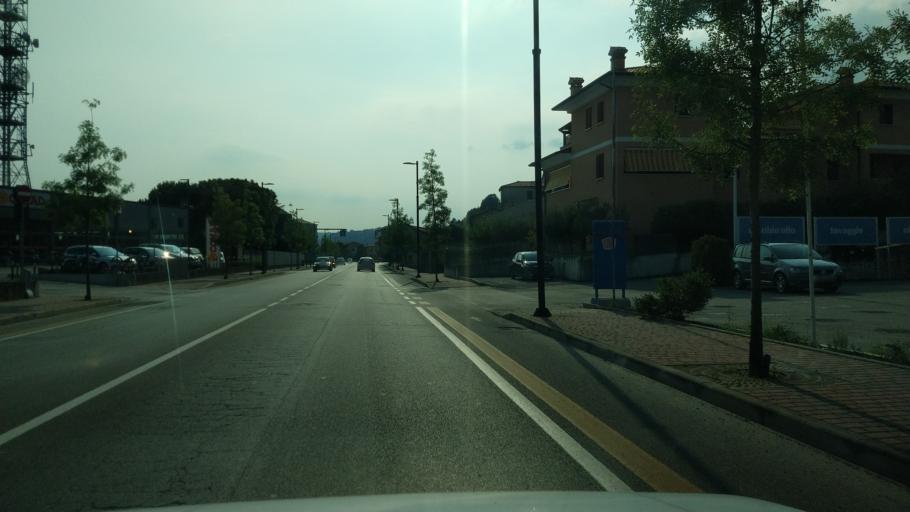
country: IT
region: Veneto
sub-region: Provincia di Vicenza
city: Bassano del Grappa
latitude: 45.7650
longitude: 11.7212
